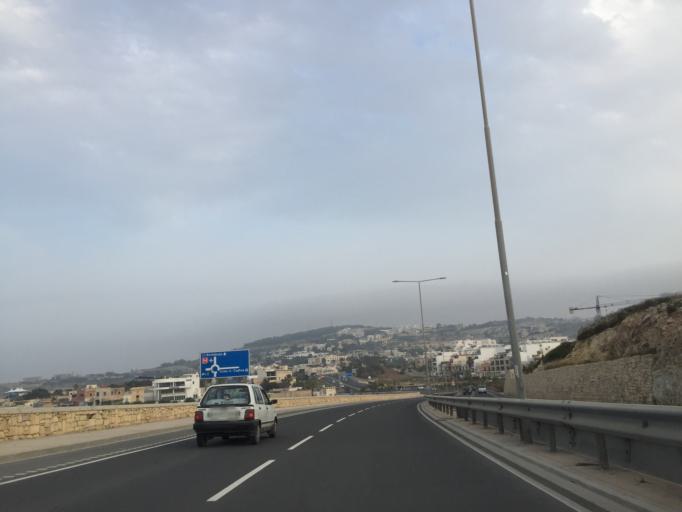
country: MT
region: Hal Gharghur
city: Hal Gharghur
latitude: 35.9420
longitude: 14.4541
